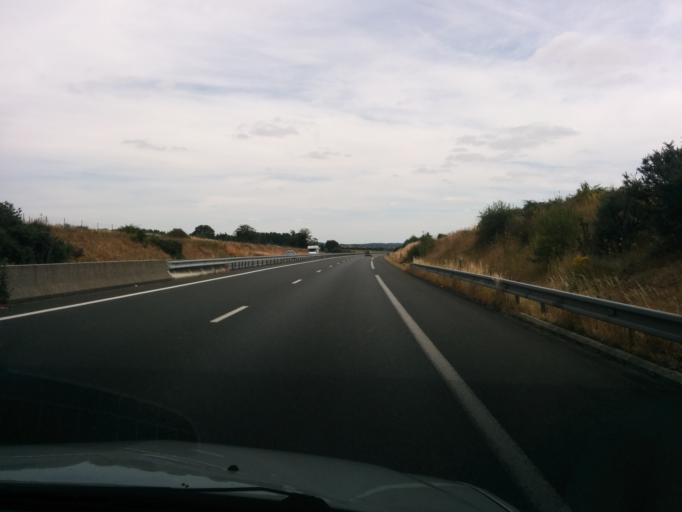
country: FR
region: Poitou-Charentes
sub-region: Departement des Deux-Sevres
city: Combrand
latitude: 46.9234
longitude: -0.7040
